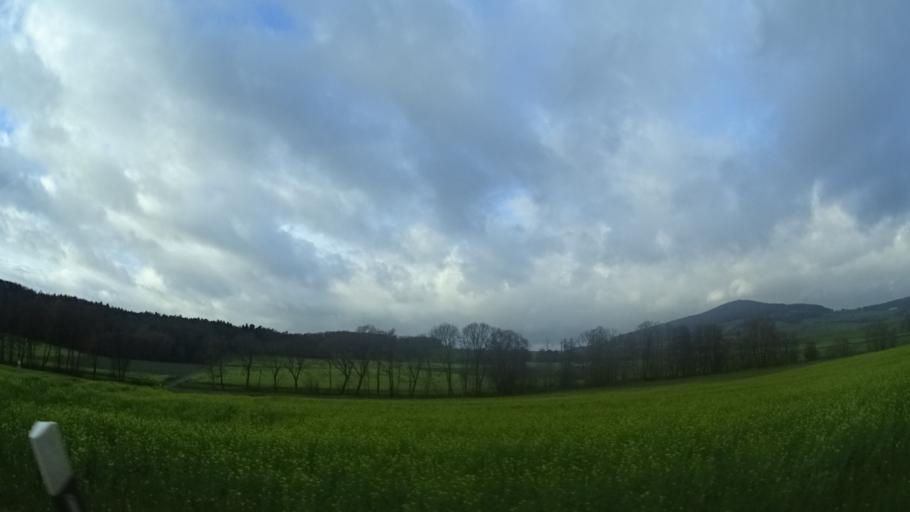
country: DE
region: Hesse
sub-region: Regierungsbezirk Kassel
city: Rasdorf
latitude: 50.7526
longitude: 9.8839
